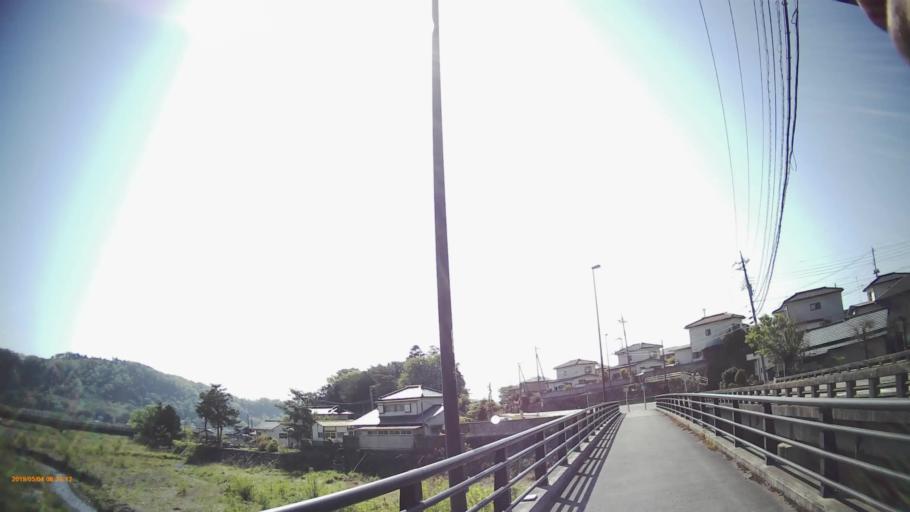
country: JP
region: Yamanashi
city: Nirasaki
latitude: 35.7322
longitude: 138.4110
